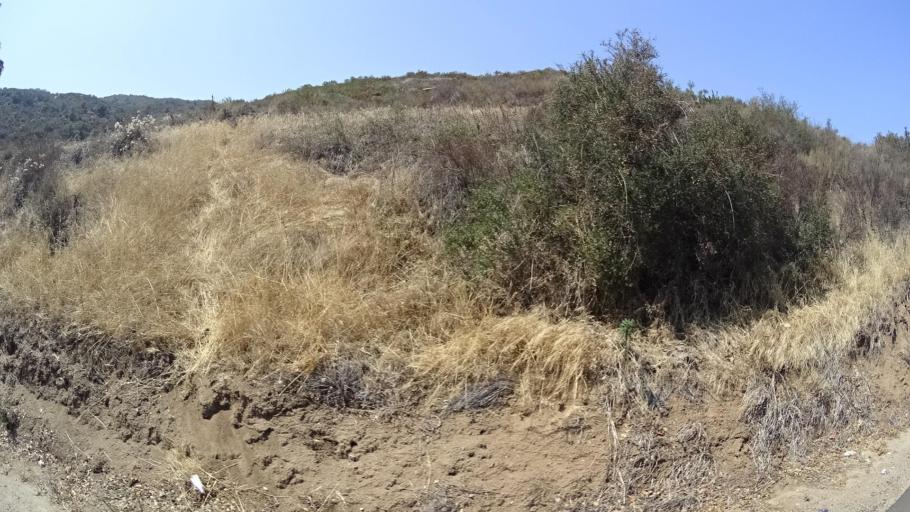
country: US
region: California
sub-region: San Diego County
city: Bonsall
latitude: 33.2716
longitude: -117.1749
